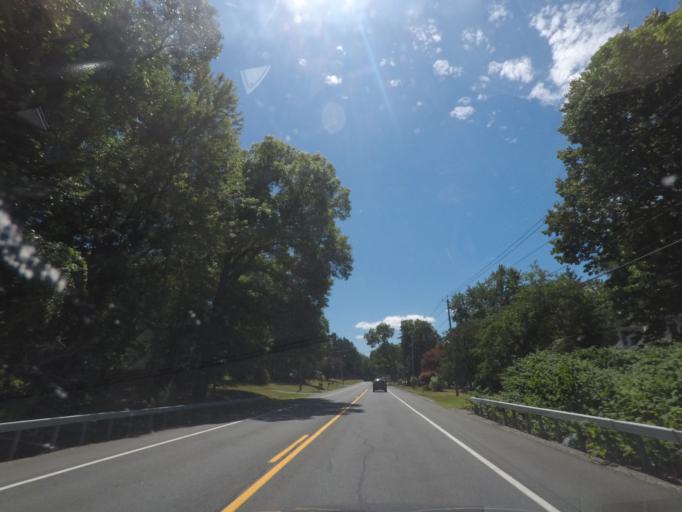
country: US
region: New York
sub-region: Albany County
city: Menands
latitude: 42.6655
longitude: -73.6915
